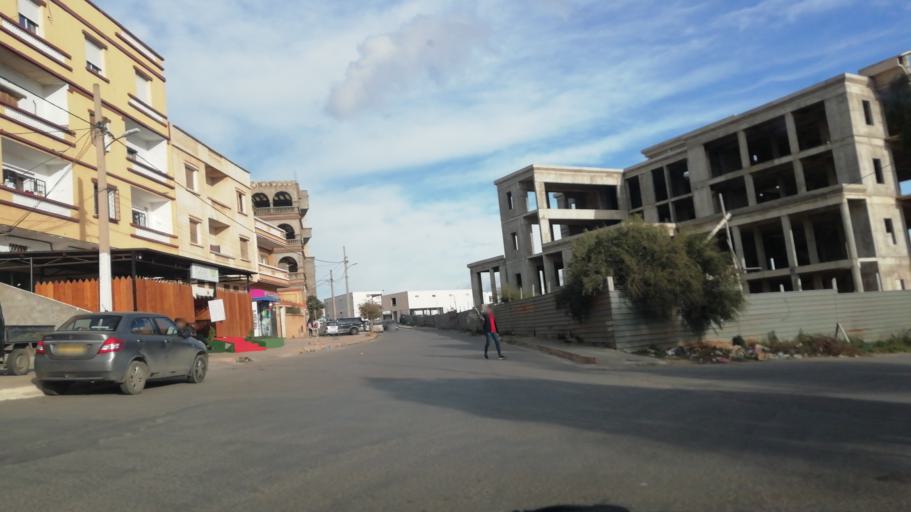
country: DZ
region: Oran
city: Bir el Djir
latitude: 35.7296
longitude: -0.5691
